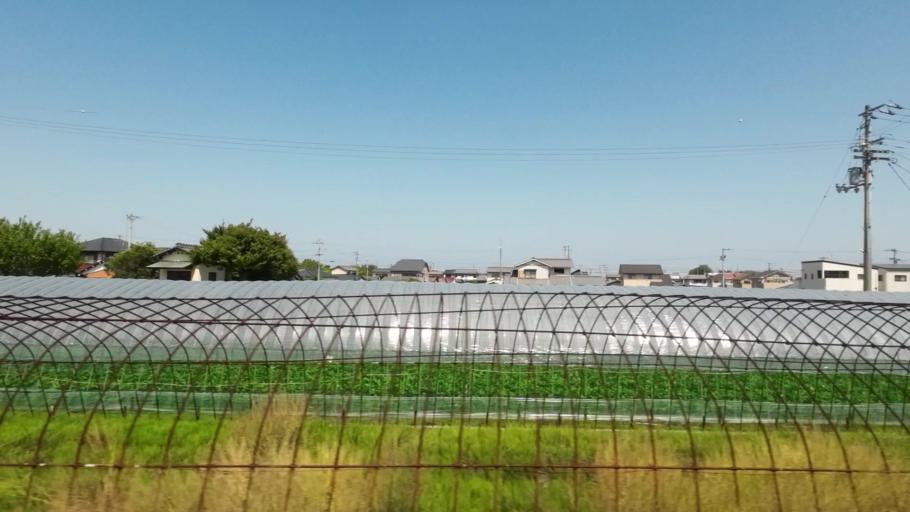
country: JP
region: Ehime
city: Niihama
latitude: 33.9643
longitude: 133.3146
